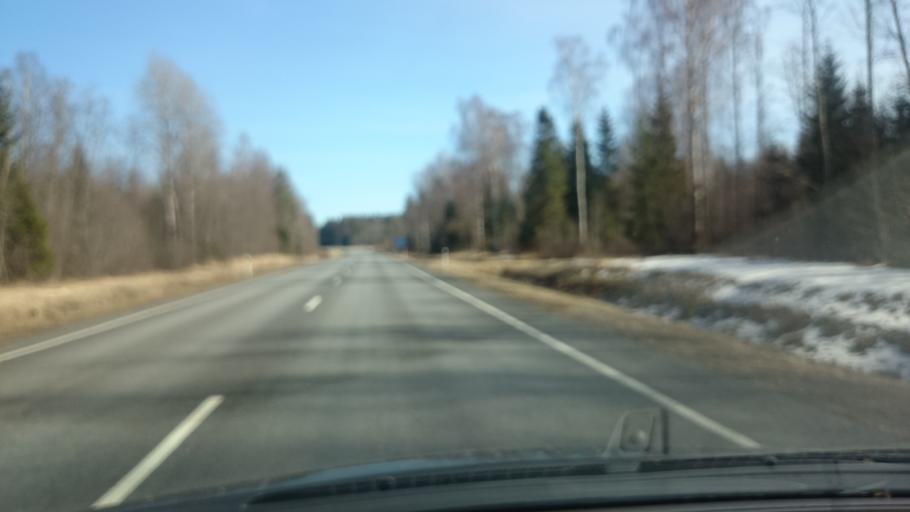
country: EE
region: Paernumaa
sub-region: Vaendra vald (alev)
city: Vandra
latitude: 58.6689
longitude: 25.0740
